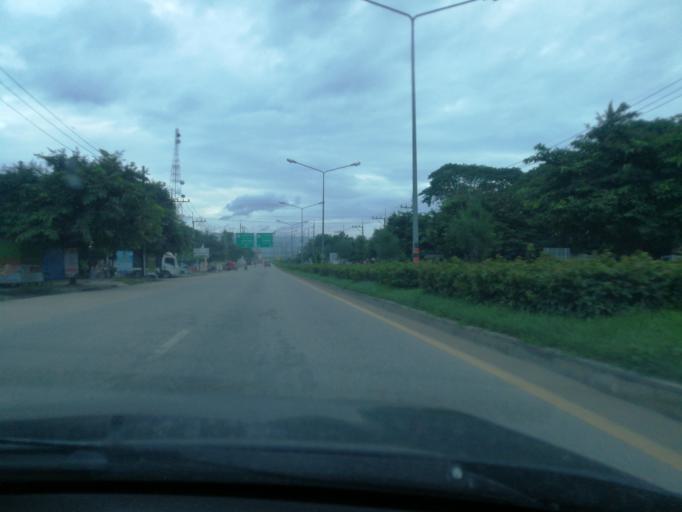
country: TH
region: Chiang Mai
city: Hot
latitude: 18.1904
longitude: 98.6123
